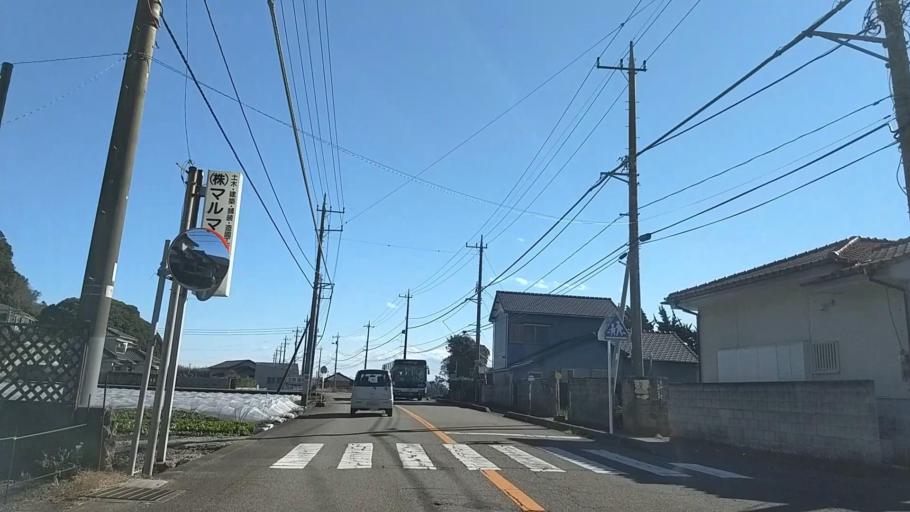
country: JP
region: Chiba
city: Tateyama
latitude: 34.9098
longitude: 139.8733
